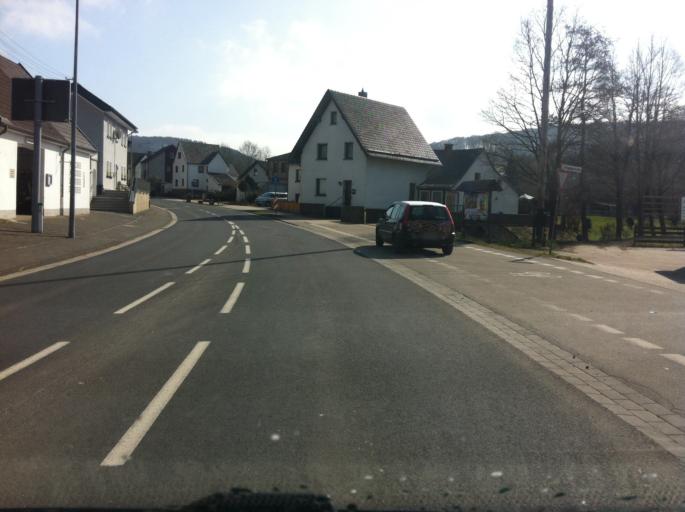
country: DE
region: North Rhine-Westphalia
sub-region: Regierungsbezirk Koln
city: Bad Munstereifel
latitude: 50.5329
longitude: 6.7704
